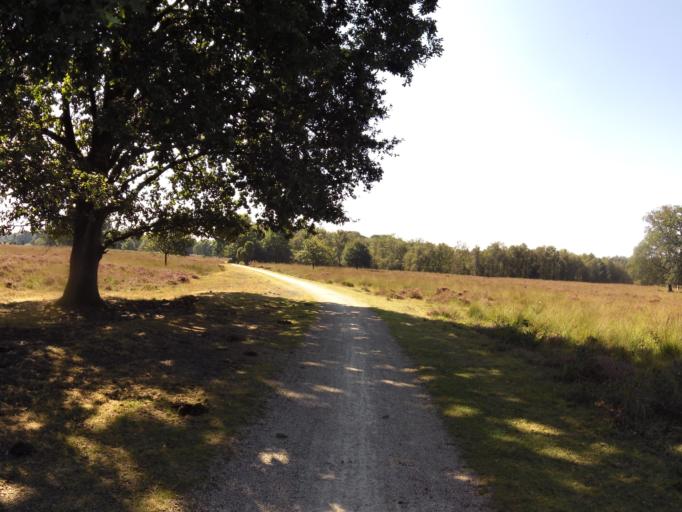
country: NL
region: Overijssel
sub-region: Gemeente Haaksbergen
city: Haaksbergen
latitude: 52.1591
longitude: 6.7989
